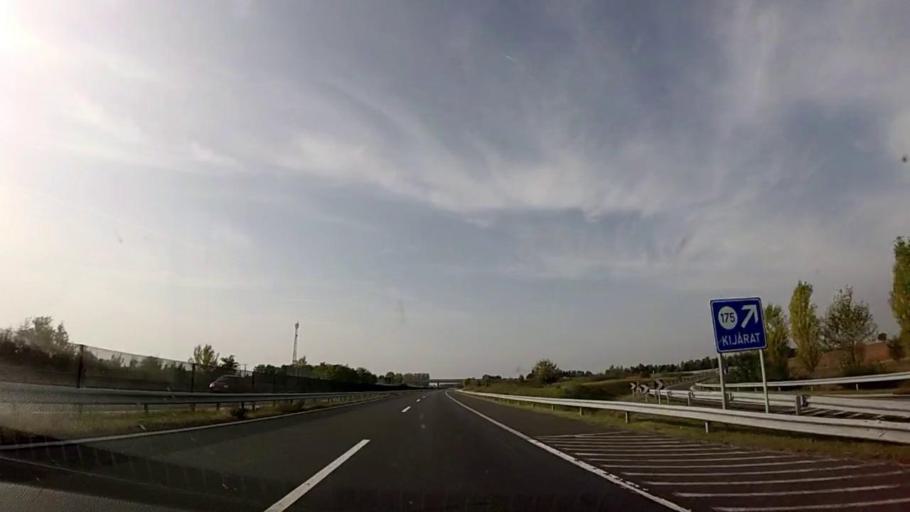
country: HU
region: Somogy
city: Balatonbereny
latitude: 46.6514
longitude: 17.3024
